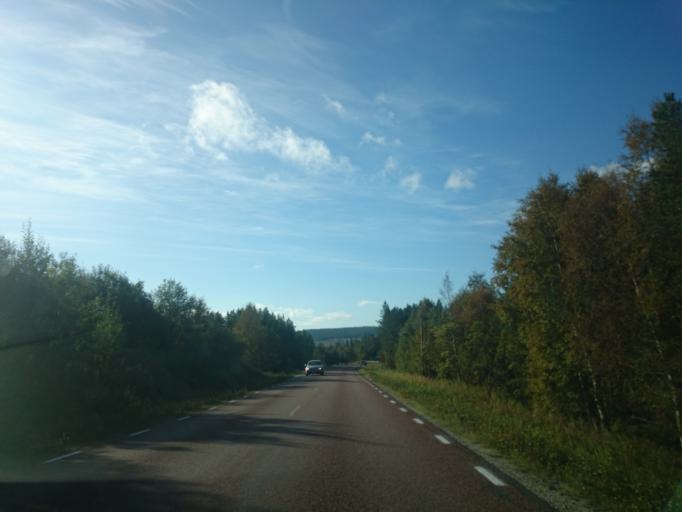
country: SE
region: Jaemtland
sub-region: Are Kommun
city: Are
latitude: 62.5588
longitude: 12.5673
